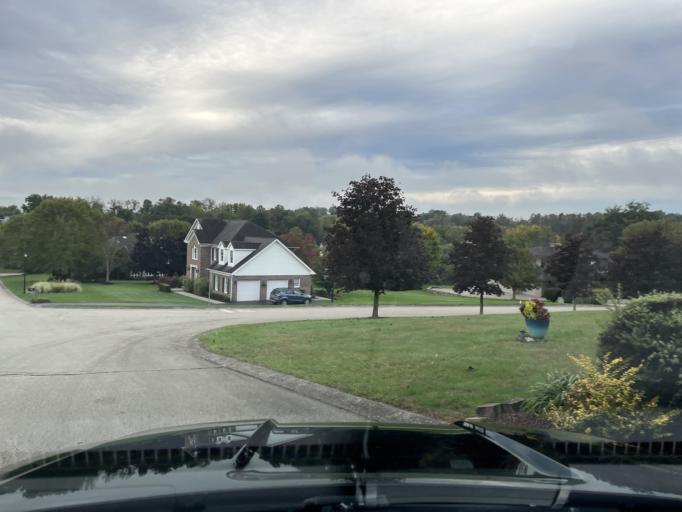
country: US
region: Pennsylvania
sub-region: Fayette County
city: Leith-Hatfield
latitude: 39.8765
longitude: -79.7296
